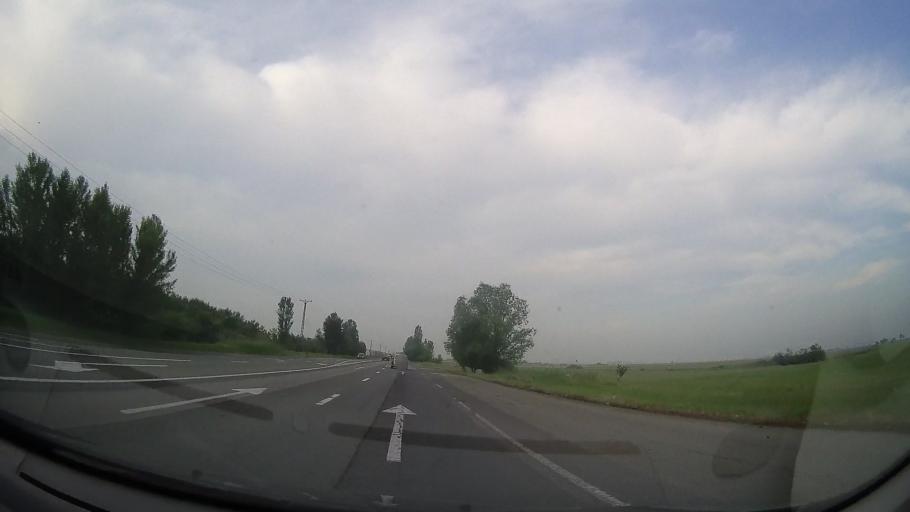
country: RO
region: Timis
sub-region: Comuna Giroc
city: Chisoda
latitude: 45.6930
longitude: 21.1758
